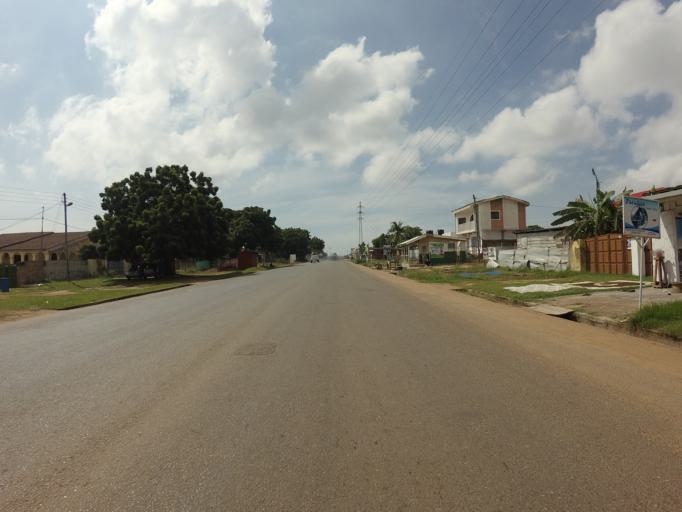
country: GH
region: Greater Accra
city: Nungua
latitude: 5.6150
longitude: -0.0917
